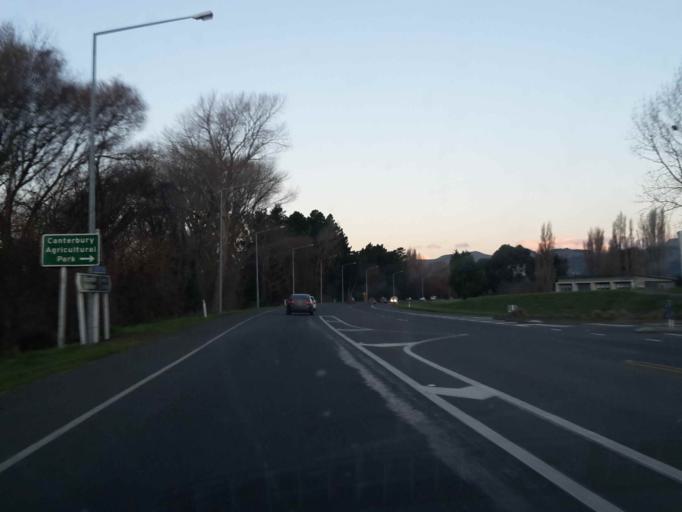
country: NZ
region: Canterbury
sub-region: Christchurch City
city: Christchurch
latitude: -43.5501
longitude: 172.5853
